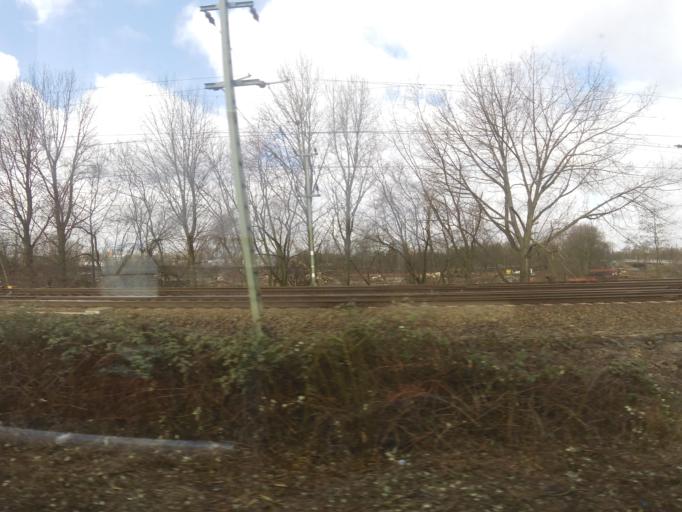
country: DE
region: Hamburg
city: Harburg
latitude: 53.4797
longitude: 10.0016
